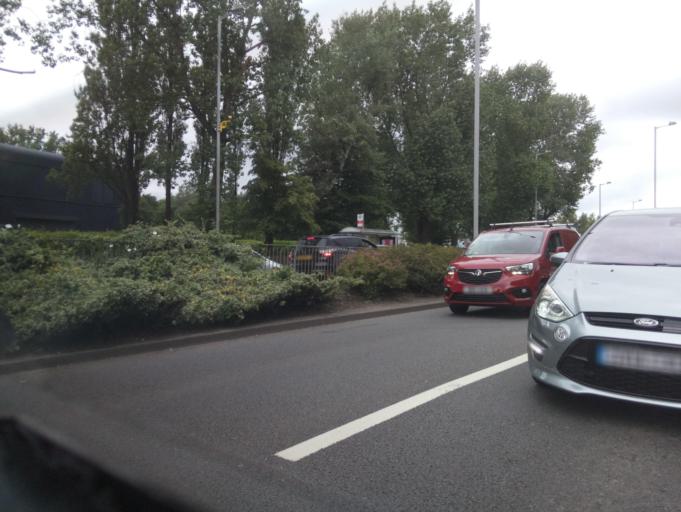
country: GB
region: England
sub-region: Wolverhampton
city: Wolverhampton
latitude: 52.5970
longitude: -2.1292
